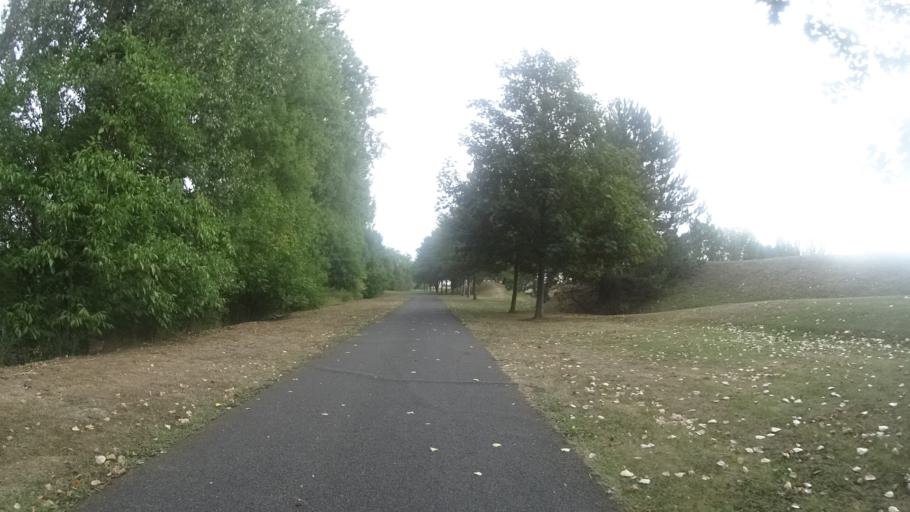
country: FR
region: Picardie
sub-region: Departement de l'Oise
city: Lacroix-Saint-Ouen
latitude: 49.3692
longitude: 2.7722
